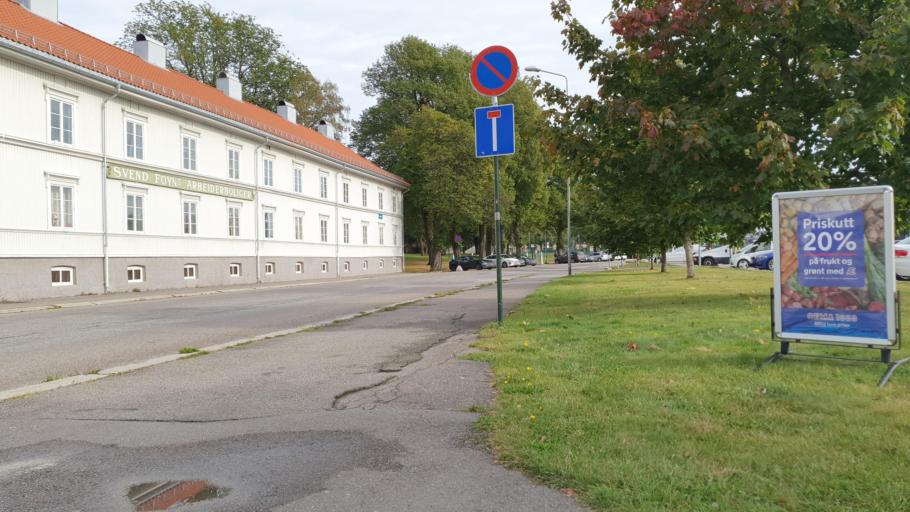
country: NO
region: Vestfold
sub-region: Tonsberg
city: Tonsberg
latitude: 59.2645
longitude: 10.4132
